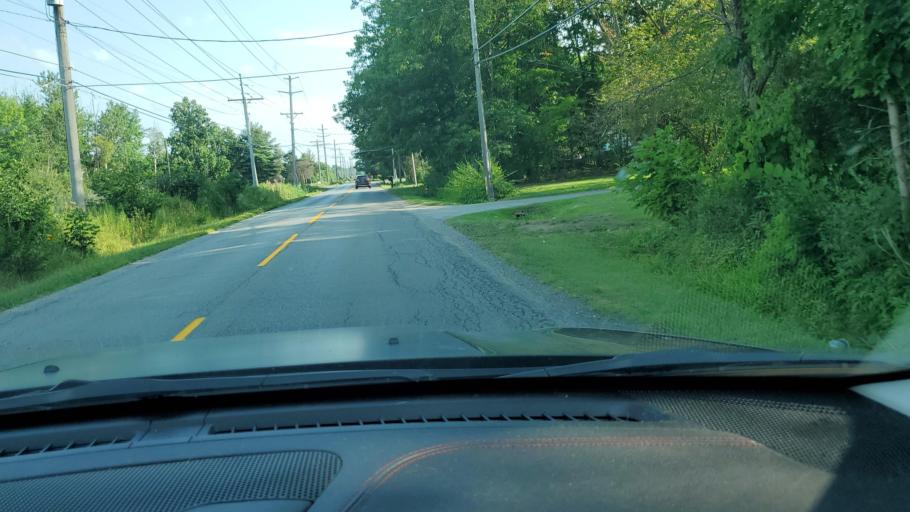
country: US
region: Ohio
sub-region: Mahoning County
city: Boardman
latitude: 41.0016
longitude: -80.6533
